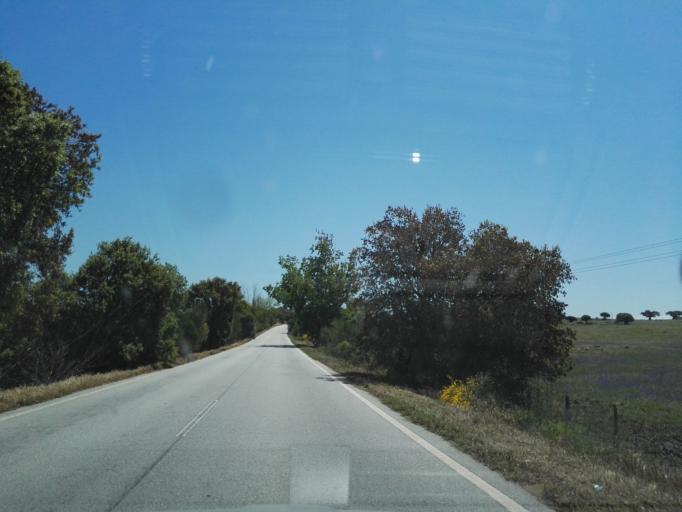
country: PT
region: Portalegre
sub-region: Arronches
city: Arronches
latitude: 39.0071
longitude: -7.2339
